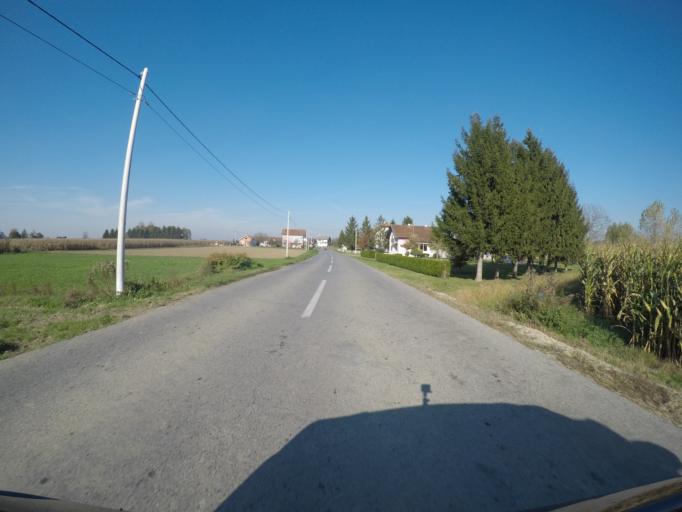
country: HR
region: Bjelovarsko-Bilogorska
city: Predavac
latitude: 45.9176
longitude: 16.7865
